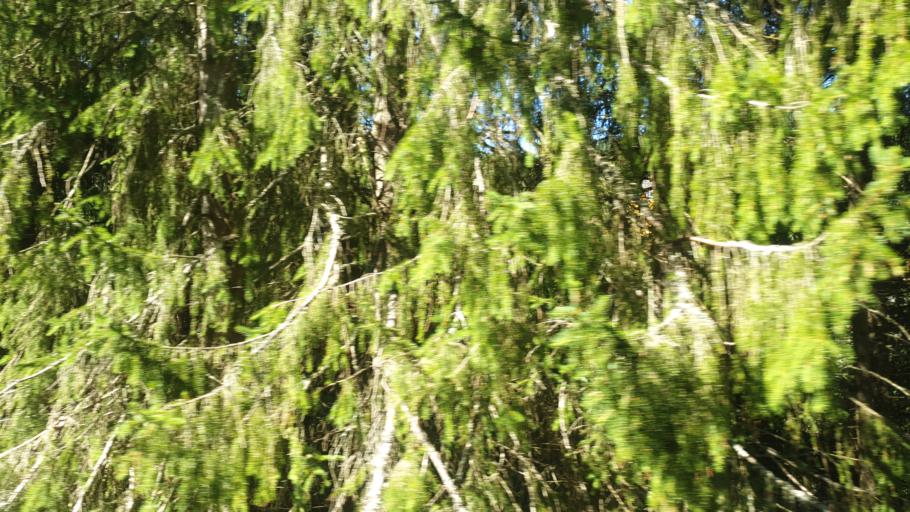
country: NO
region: Sor-Trondelag
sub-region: Meldal
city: Meldal
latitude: 63.1377
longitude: 9.7112
